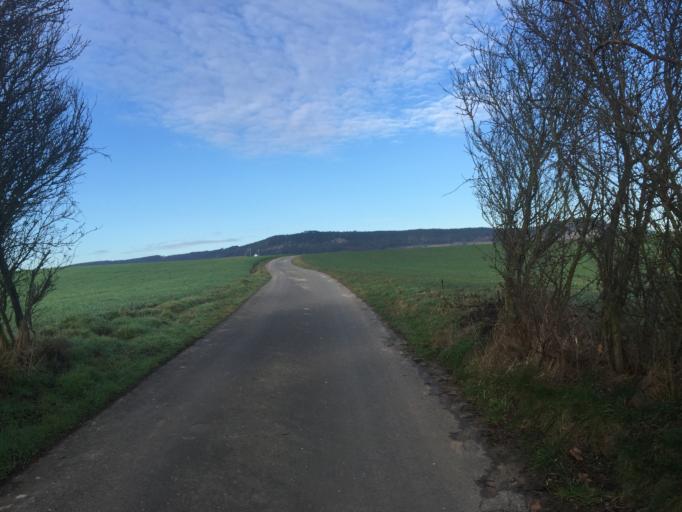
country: DE
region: Thuringia
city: Orlamunde
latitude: 50.7591
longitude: 11.5007
